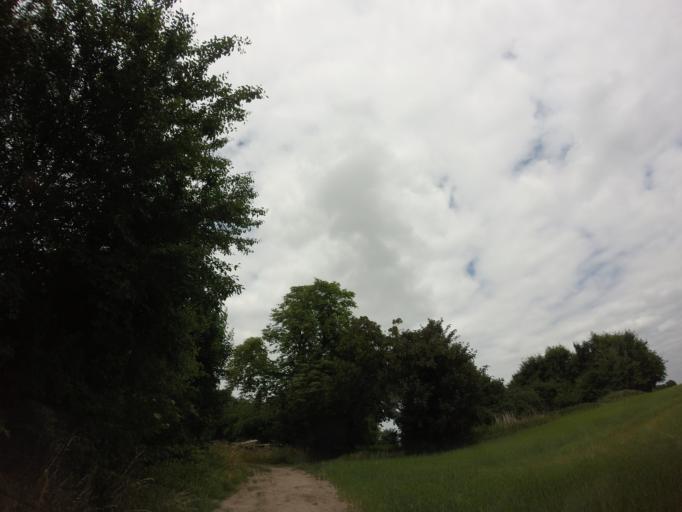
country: PL
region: West Pomeranian Voivodeship
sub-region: Powiat choszczenski
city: Krzecin
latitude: 53.0736
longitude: 15.5268
